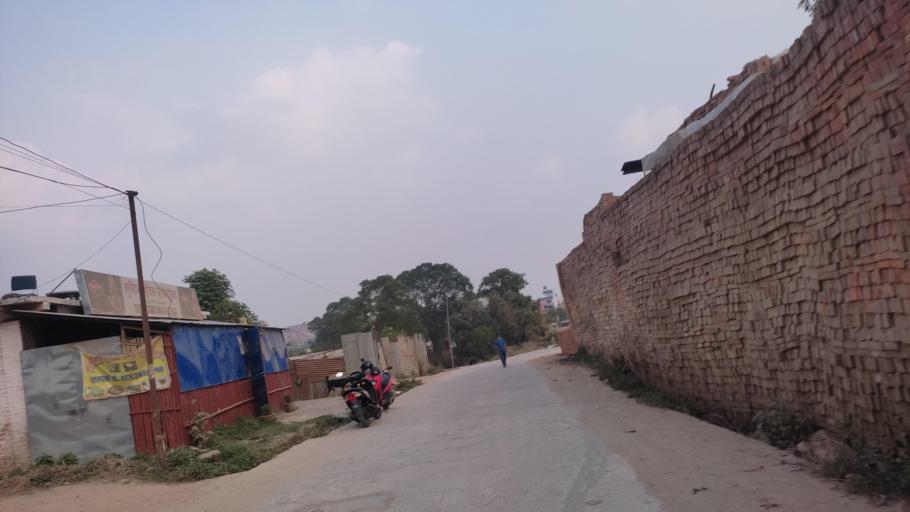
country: NP
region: Central Region
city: Kirtipur
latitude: 27.6824
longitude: 85.2593
